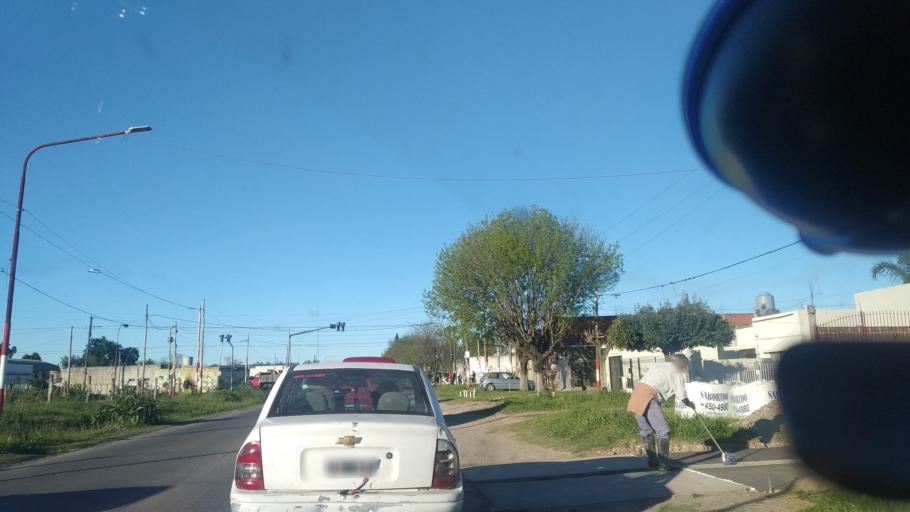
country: AR
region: Buenos Aires
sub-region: Partido de La Plata
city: La Plata
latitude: -34.9602
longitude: -57.9598
